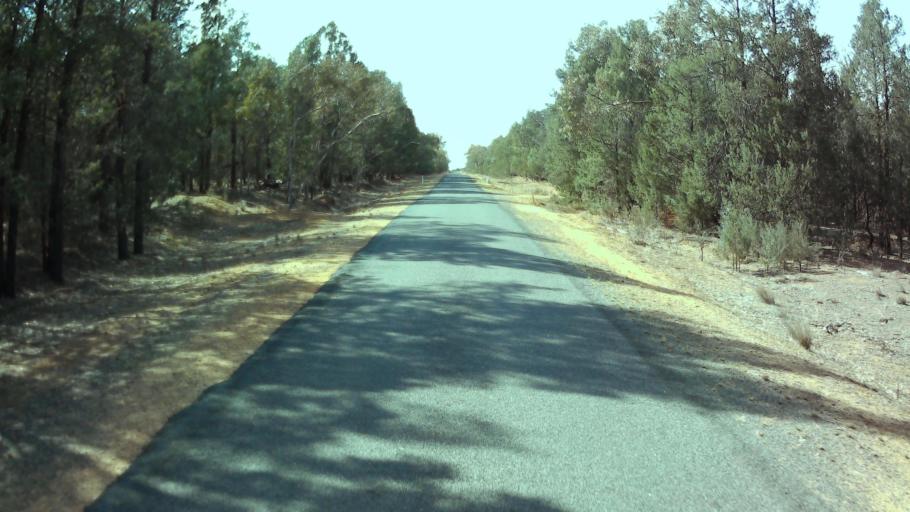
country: AU
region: New South Wales
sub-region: Weddin
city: Grenfell
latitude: -33.7303
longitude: 148.0358
